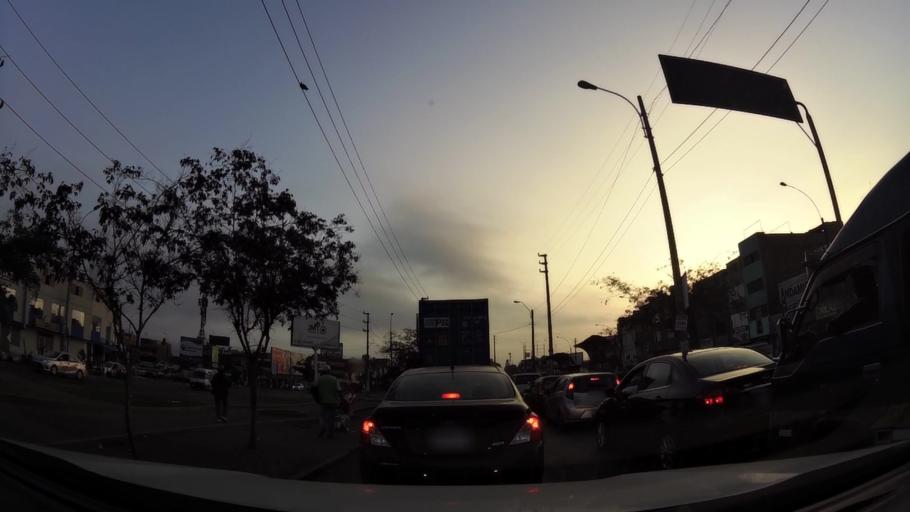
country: PE
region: Lima
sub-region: Lima
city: Independencia
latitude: -12.0124
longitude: -77.0789
